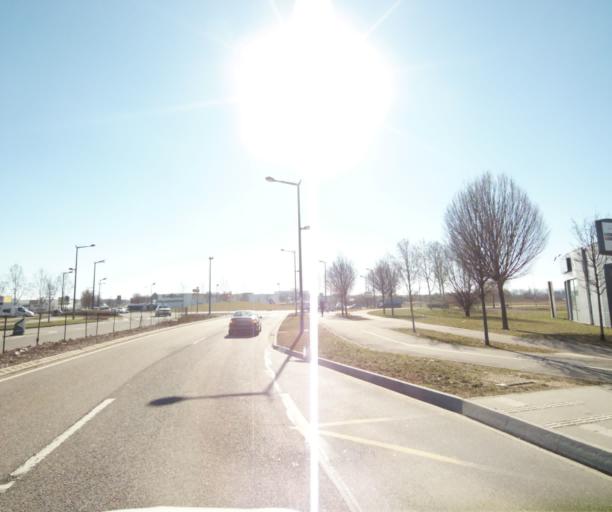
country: FR
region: Lorraine
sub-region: Departement de Meurthe-et-Moselle
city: Pulnoy
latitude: 48.7090
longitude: 6.2438
